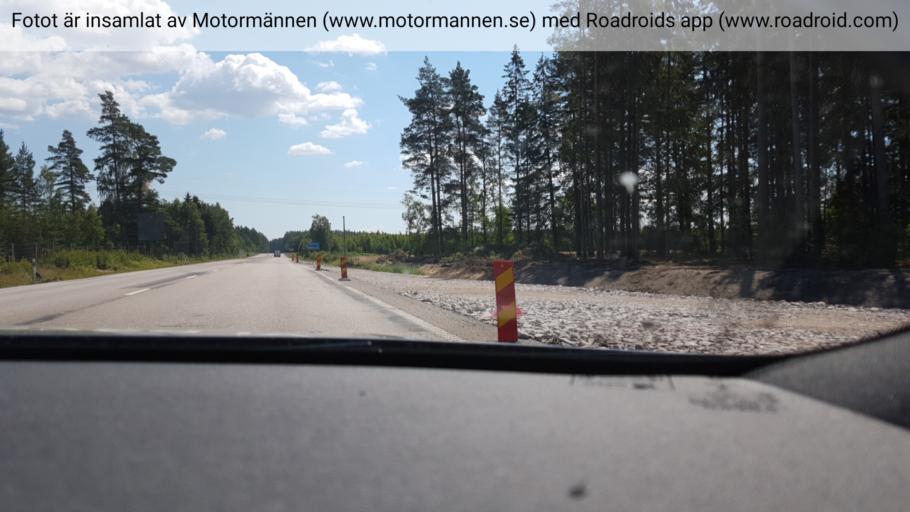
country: SE
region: Vaestra Goetaland
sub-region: Lidkopings Kommun
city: Lidkoping
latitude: 58.4789
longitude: 13.2025
